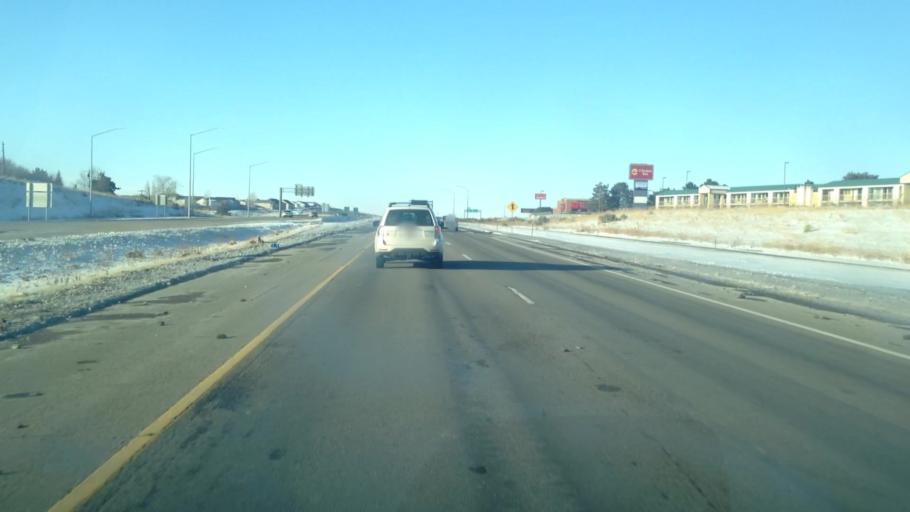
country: US
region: Idaho
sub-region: Bannock County
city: Pocatello
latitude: 42.8985
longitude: -112.4359
